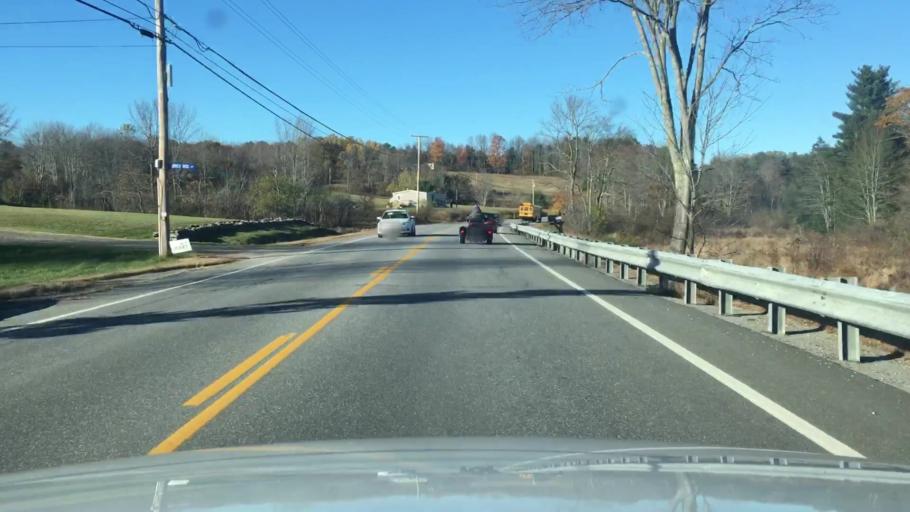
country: US
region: Maine
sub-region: Sagadahoc County
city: Topsham
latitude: 44.0347
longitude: -69.9434
